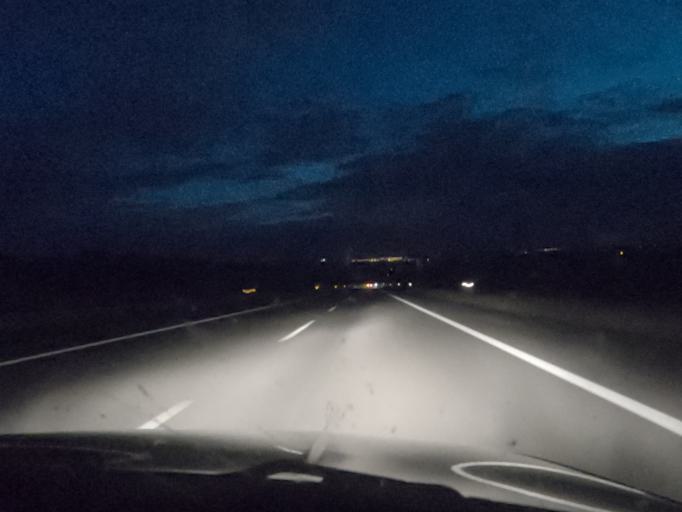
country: PT
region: Portalegre
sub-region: Elvas
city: Elvas
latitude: 38.8673
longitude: -7.2895
